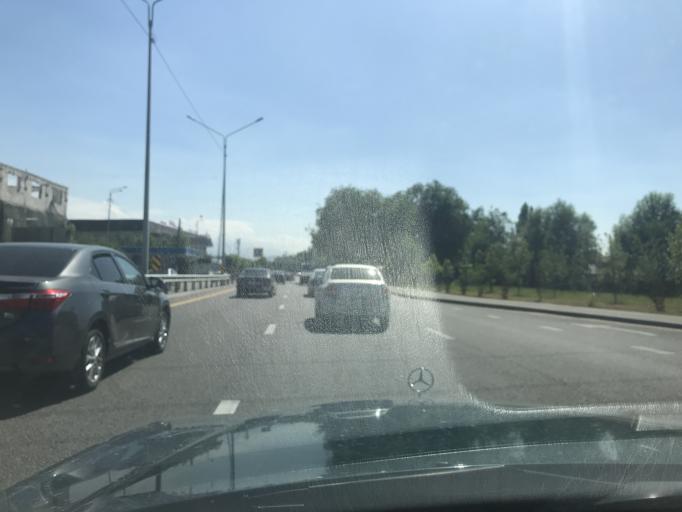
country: KZ
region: Almaty Qalasy
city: Almaty
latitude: 43.2924
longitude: 76.9931
